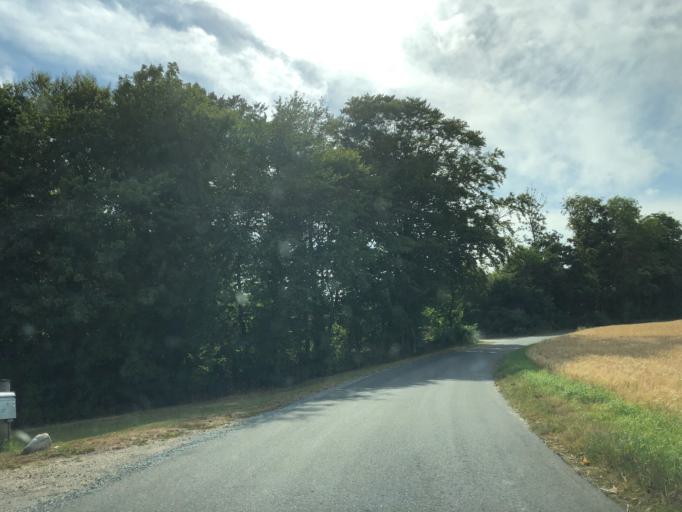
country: DK
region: South Denmark
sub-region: Vejle Kommune
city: Egtved
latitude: 55.6714
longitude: 9.2738
